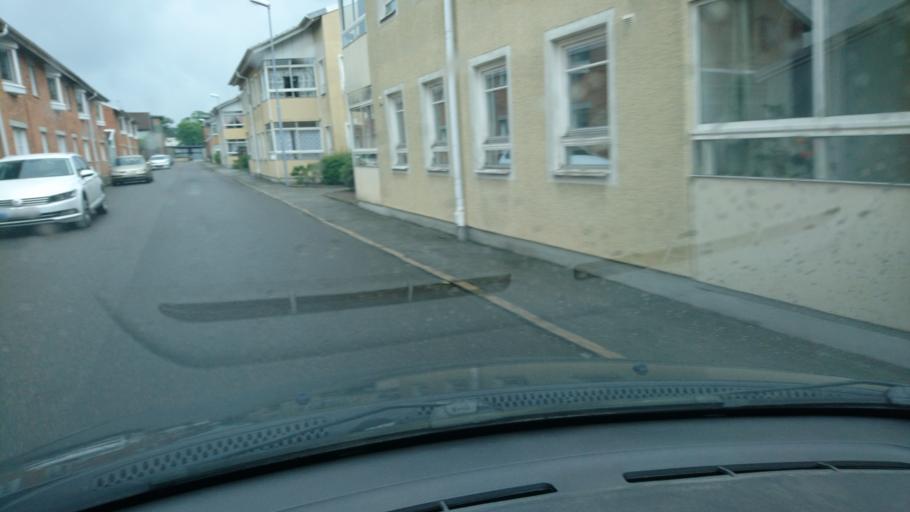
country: SE
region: Skane
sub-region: Tomelilla Kommun
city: Tomelilla
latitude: 55.5449
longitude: 13.9529
